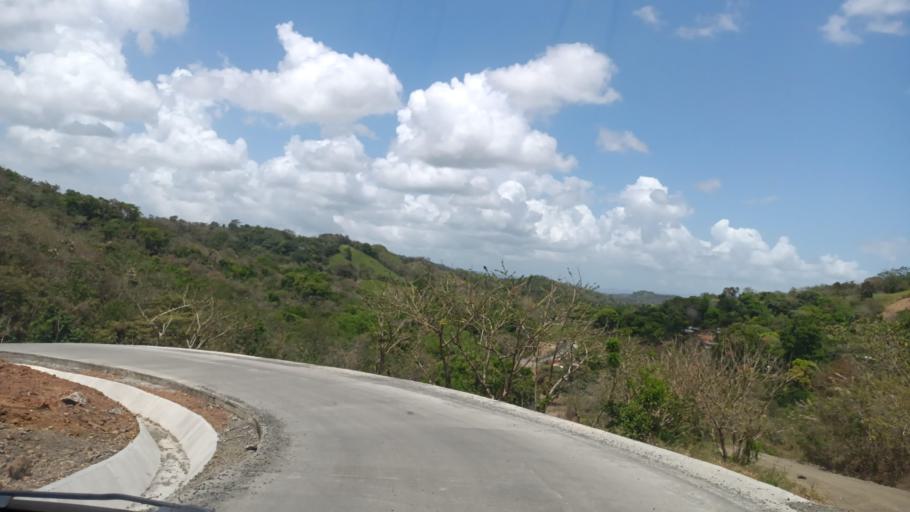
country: PA
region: Panama
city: Alcalde Diaz
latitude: 9.0785
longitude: -79.5739
